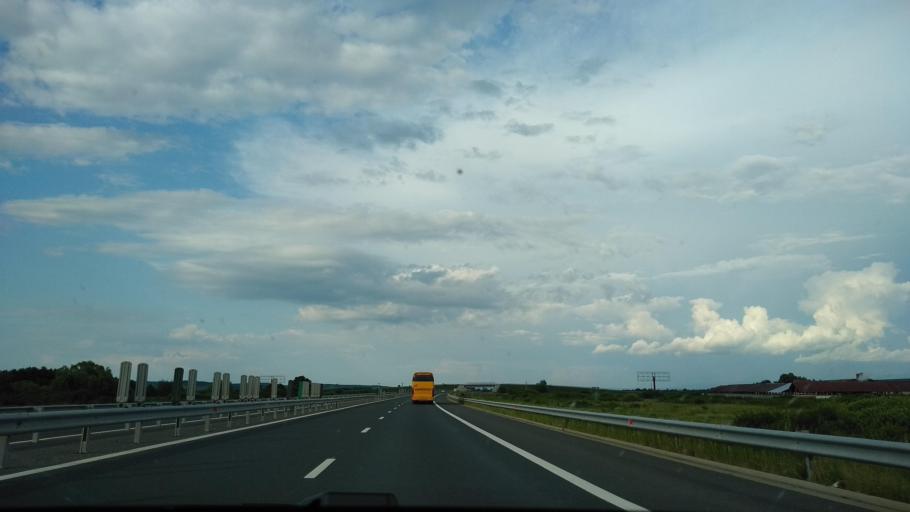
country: RO
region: Timis
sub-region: Comuna Bethausen
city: Bethausen
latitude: 45.8578
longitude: 21.9744
